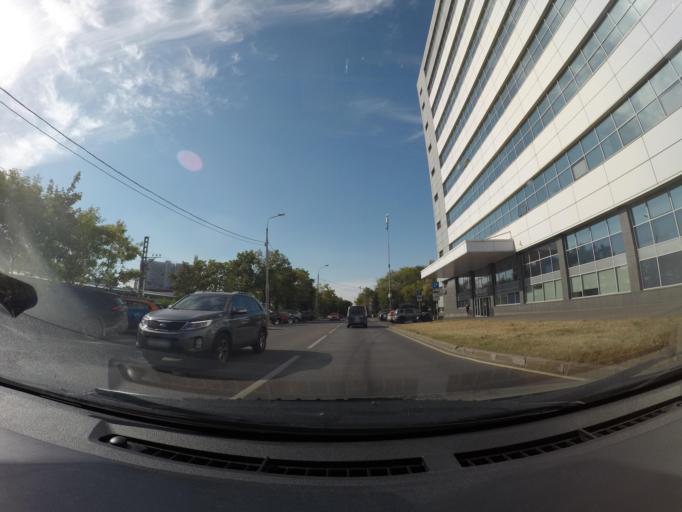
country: RU
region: Moscow
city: Mar'ina Roshcha
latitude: 55.8069
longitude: 37.6220
